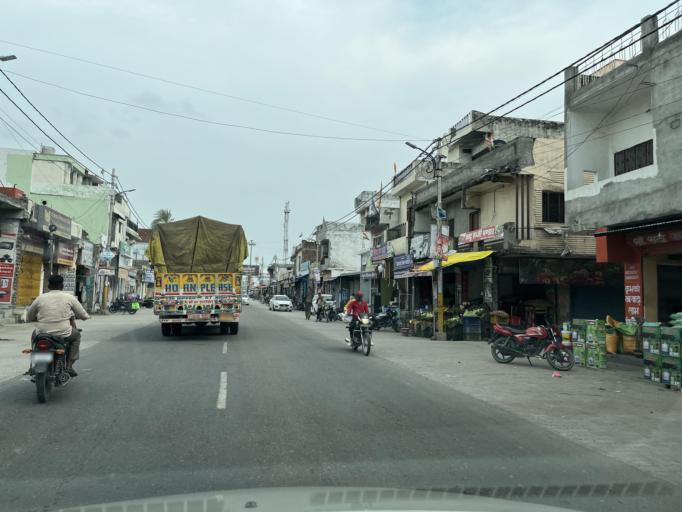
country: IN
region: Uttar Pradesh
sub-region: Rampur
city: Bilaspur
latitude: 29.0418
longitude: 79.2488
